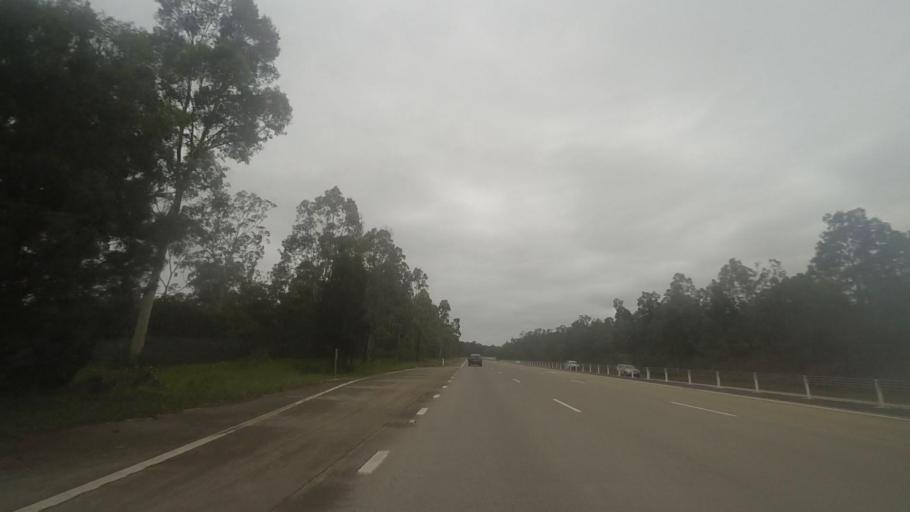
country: AU
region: New South Wales
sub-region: Port Stephens Shire
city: Medowie
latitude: -32.6890
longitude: 151.8094
